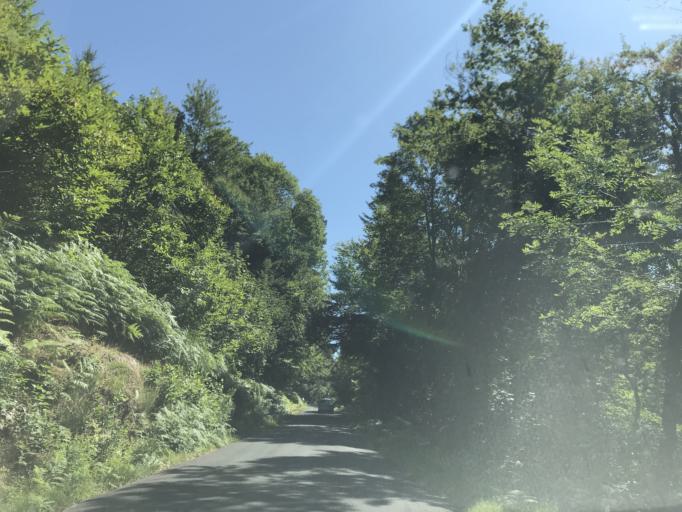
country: FR
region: Auvergne
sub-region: Departement du Puy-de-Dome
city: Job
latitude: 45.6697
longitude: 3.7356
